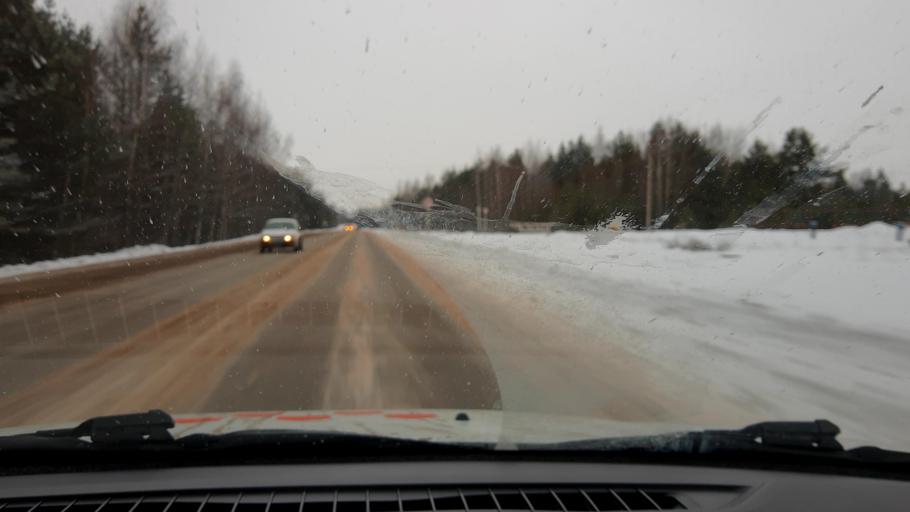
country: RU
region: Nizjnij Novgorod
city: Bor
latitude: 56.3249
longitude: 44.1412
